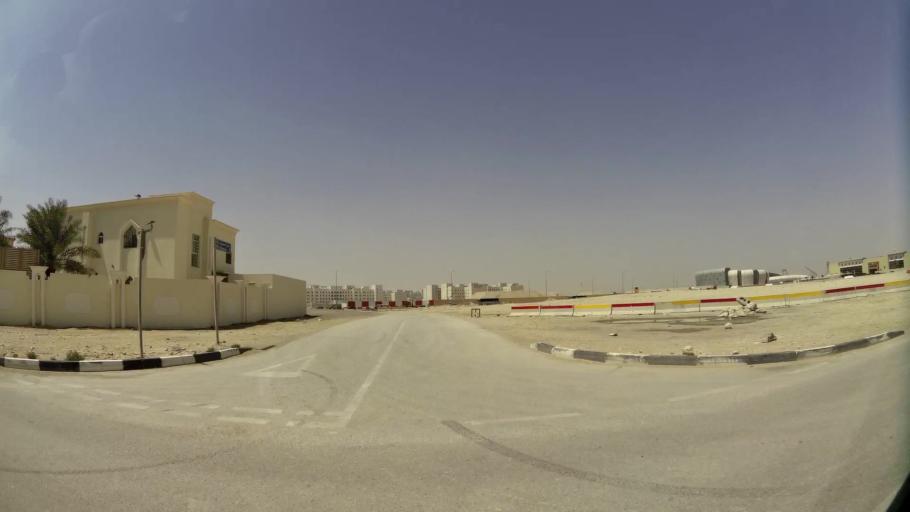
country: QA
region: Baladiyat Umm Salal
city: Umm Salal Muhammad
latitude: 25.3672
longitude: 51.4757
